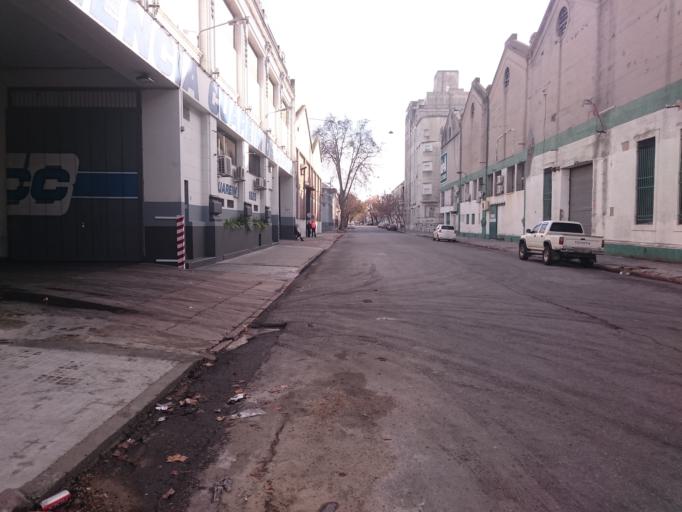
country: UY
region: Montevideo
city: Montevideo
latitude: -34.8966
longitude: -56.1912
